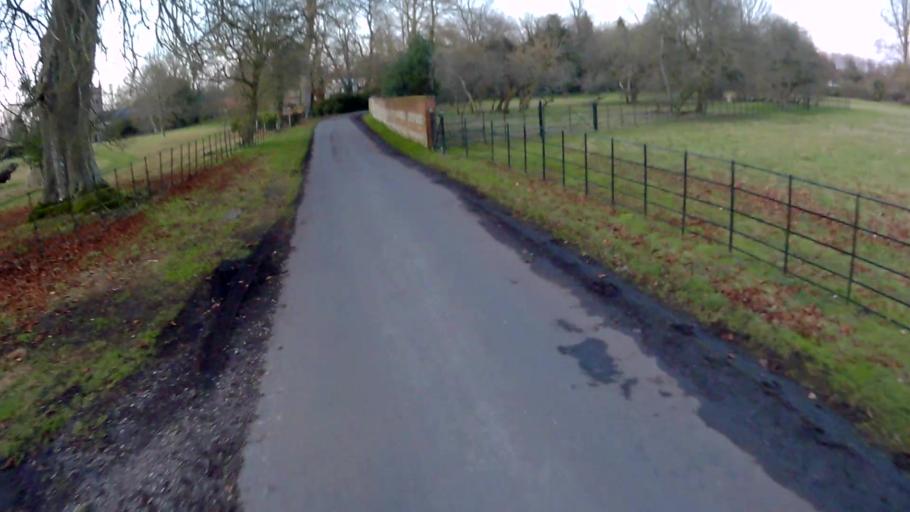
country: GB
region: England
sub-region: Hampshire
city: Overton
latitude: 51.2475
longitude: -1.2175
